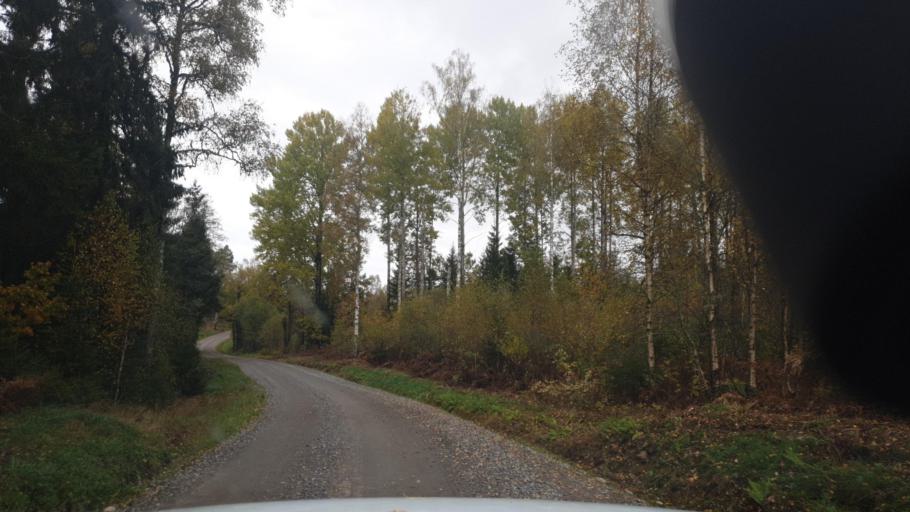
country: SE
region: Vaermland
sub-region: Karlstads Kommun
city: Edsvalla
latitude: 59.4697
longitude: 13.1269
